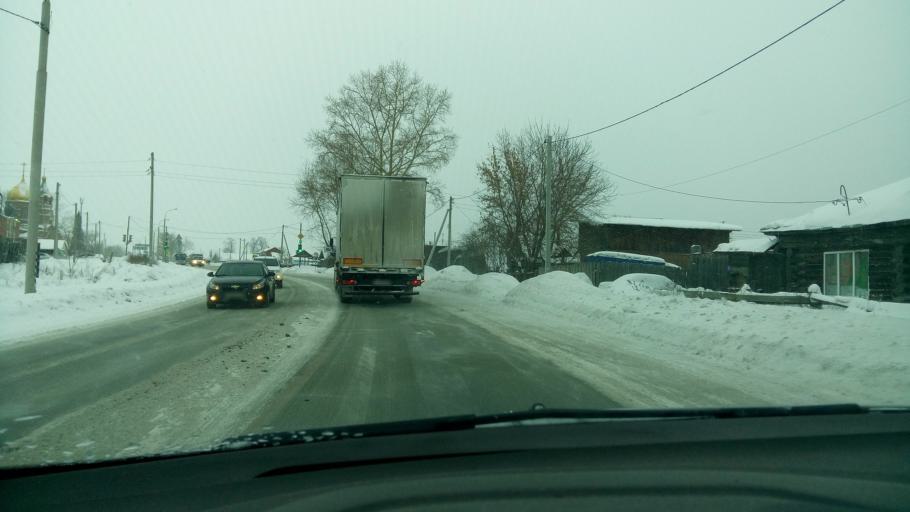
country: RU
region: Sverdlovsk
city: Zarechnyy
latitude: 56.7534
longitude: 61.3274
